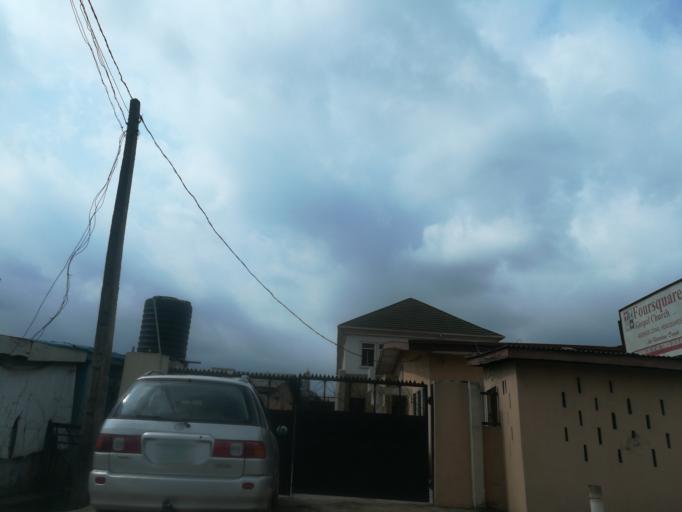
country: NG
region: Lagos
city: Ikeja
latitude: 6.6233
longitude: 3.3537
